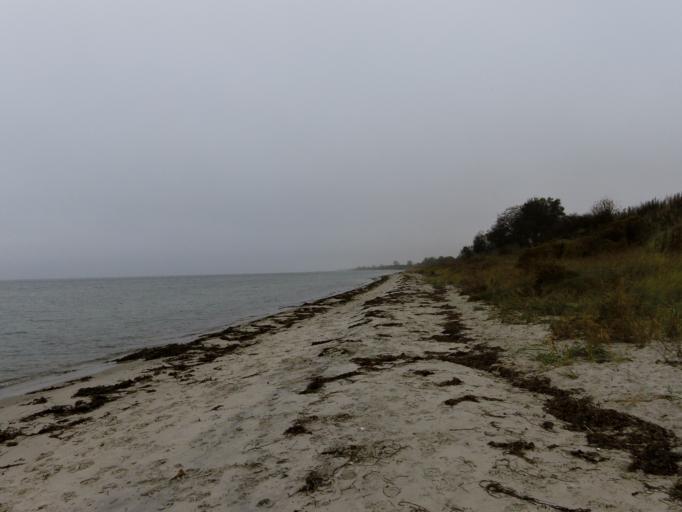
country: DK
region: Central Jutland
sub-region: Arhus Kommune
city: Malling
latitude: 55.9552
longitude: 10.2648
